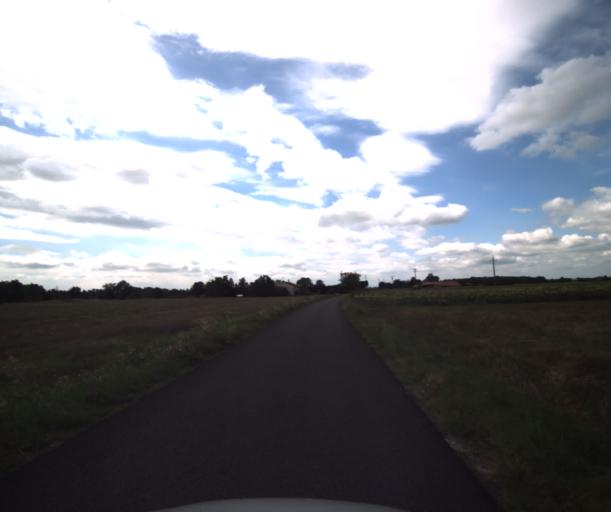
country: FR
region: Midi-Pyrenees
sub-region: Departement de la Haute-Garonne
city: Lacasse
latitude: 43.3788
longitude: 1.2532
